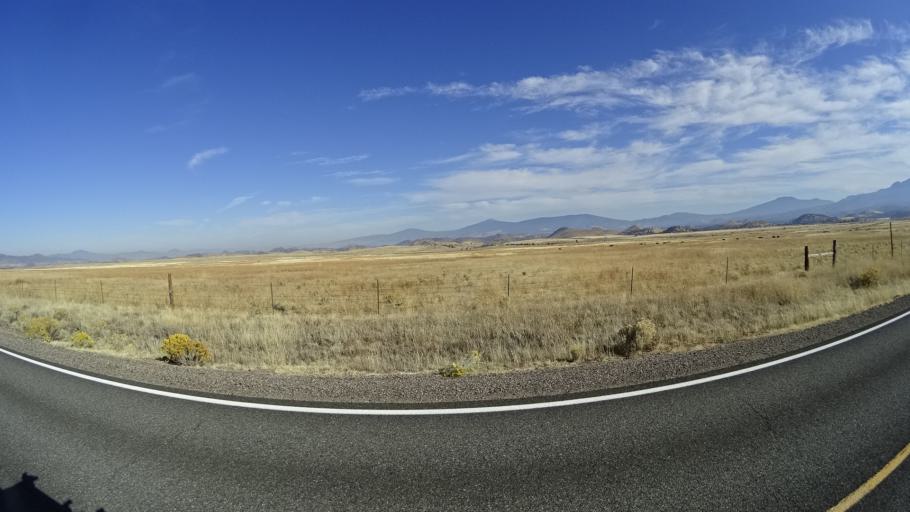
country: US
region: California
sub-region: Siskiyou County
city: Weed
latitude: 41.4763
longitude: -122.4870
